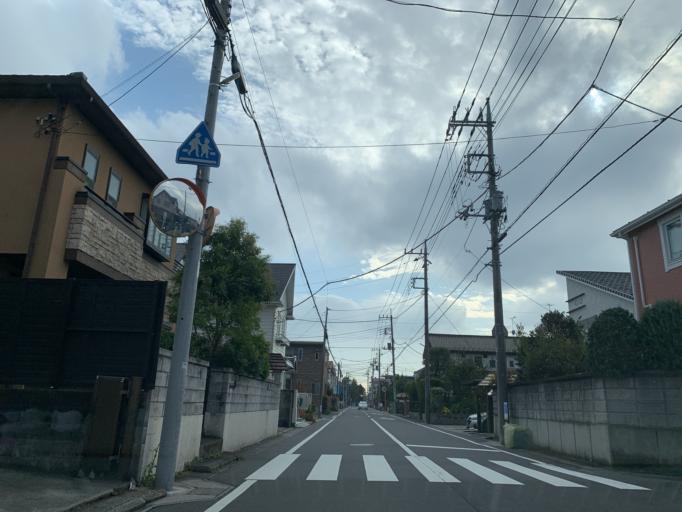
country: JP
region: Chiba
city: Nagareyama
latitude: 35.9018
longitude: 139.9139
